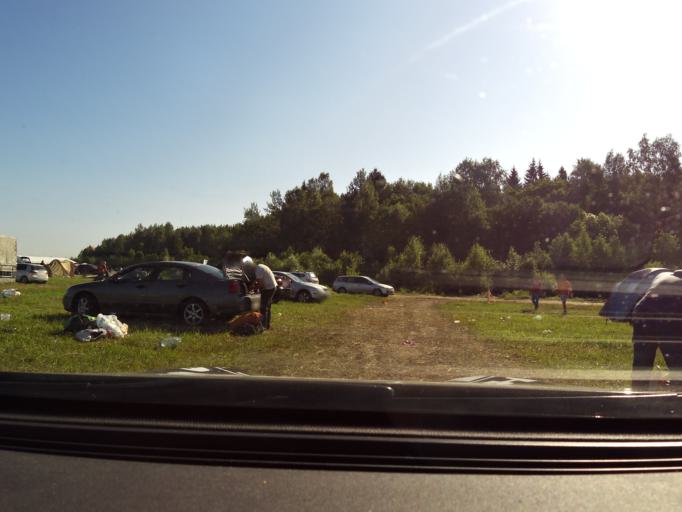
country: RU
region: Tverskaya
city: Zavidovo
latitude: 56.6025
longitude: 36.6466
